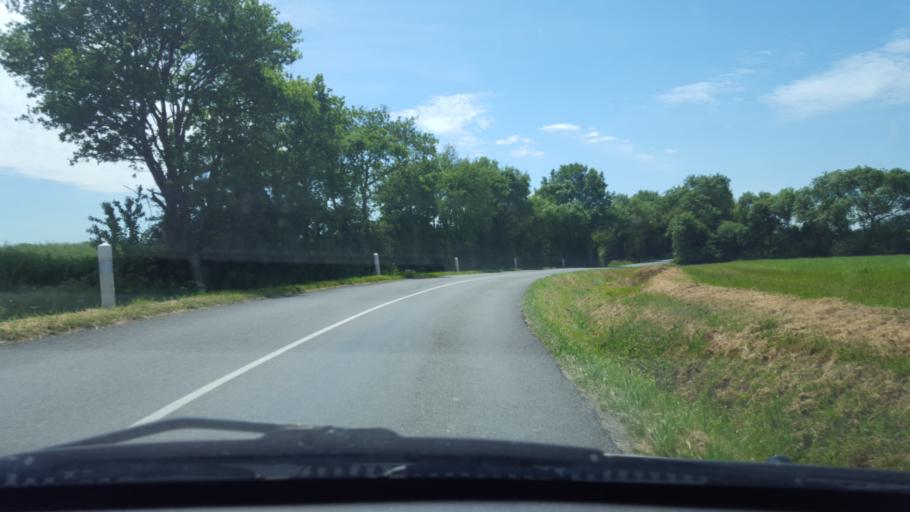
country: FR
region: Pays de la Loire
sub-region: Departement de la Loire-Atlantique
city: Saint-Philbert-de-Grand-Lieu
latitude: 46.9878
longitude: -1.6644
